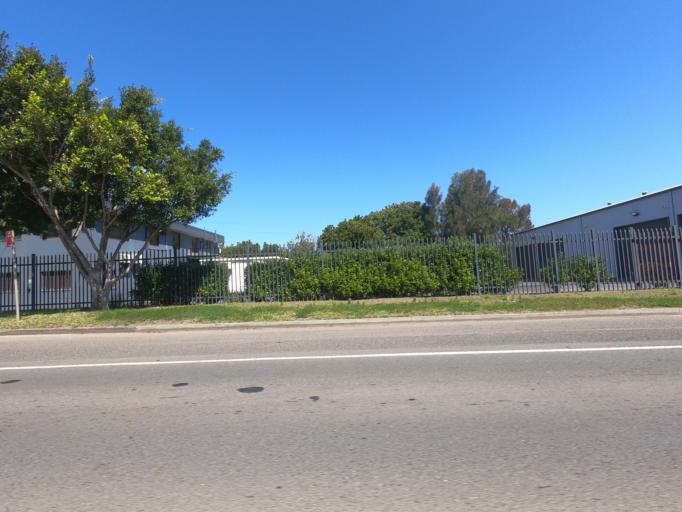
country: AU
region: New South Wales
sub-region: Wollongong
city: Koonawarra
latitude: -34.4707
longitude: 150.8145
